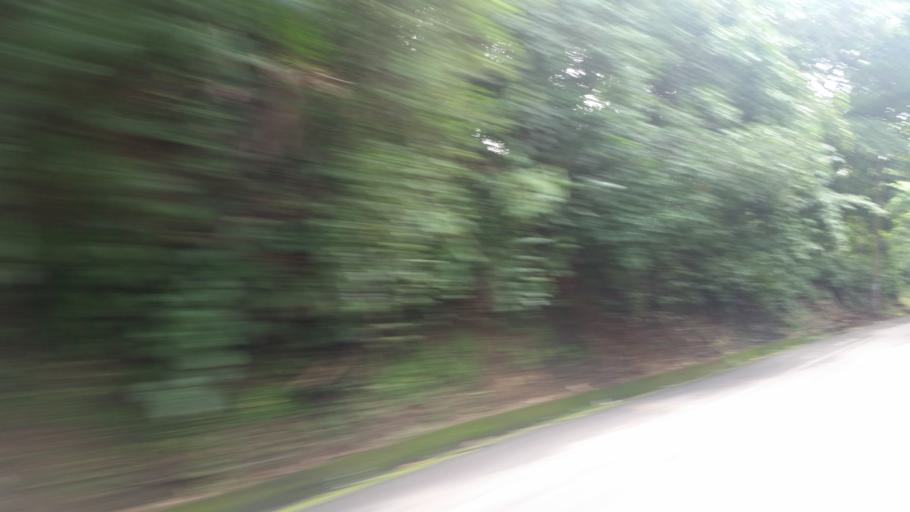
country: CO
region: Magdalena
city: Santa Marta
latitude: 11.2814
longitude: -73.9112
